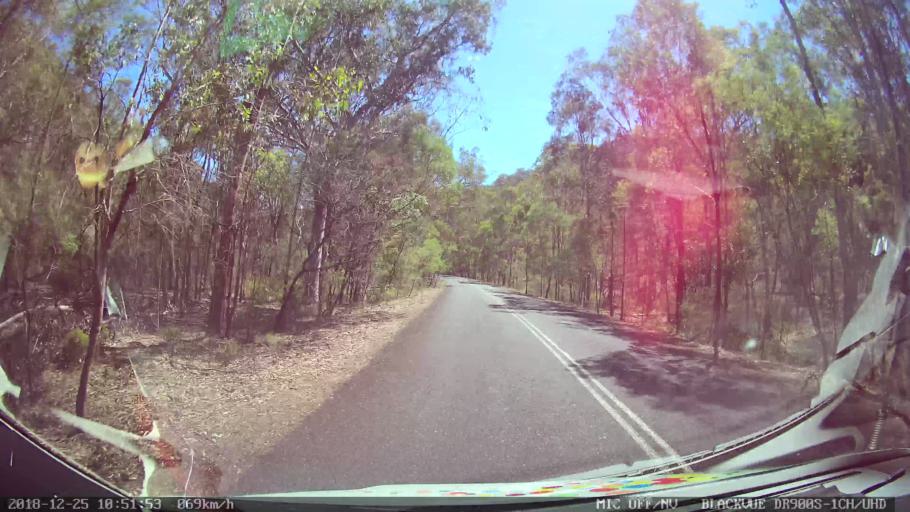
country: AU
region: New South Wales
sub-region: Upper Hunter Shire
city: Merriwa
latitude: -32.4334
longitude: 150.2716
